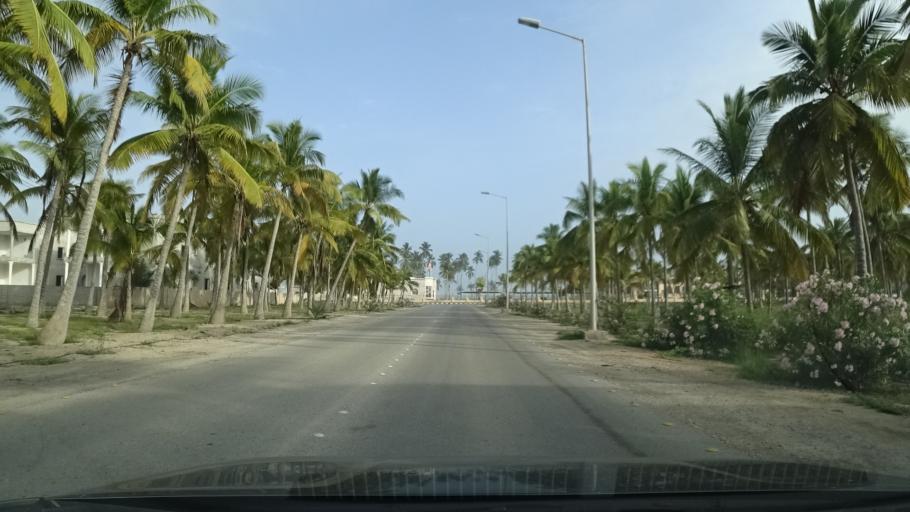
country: OM
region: Zufar
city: Salalah
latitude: 17.0108
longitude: 54.1532
